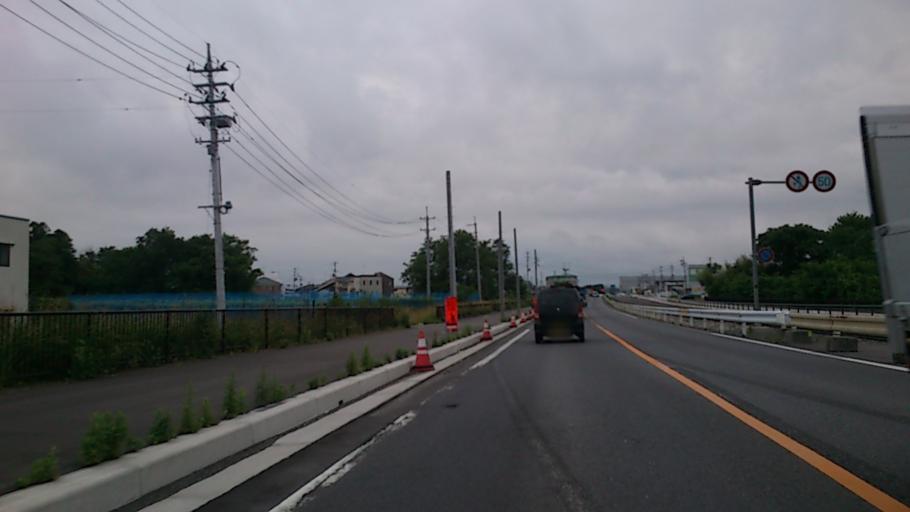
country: JP
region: Fukushima
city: Sukagawa
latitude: 37.2601
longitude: 140.3478
